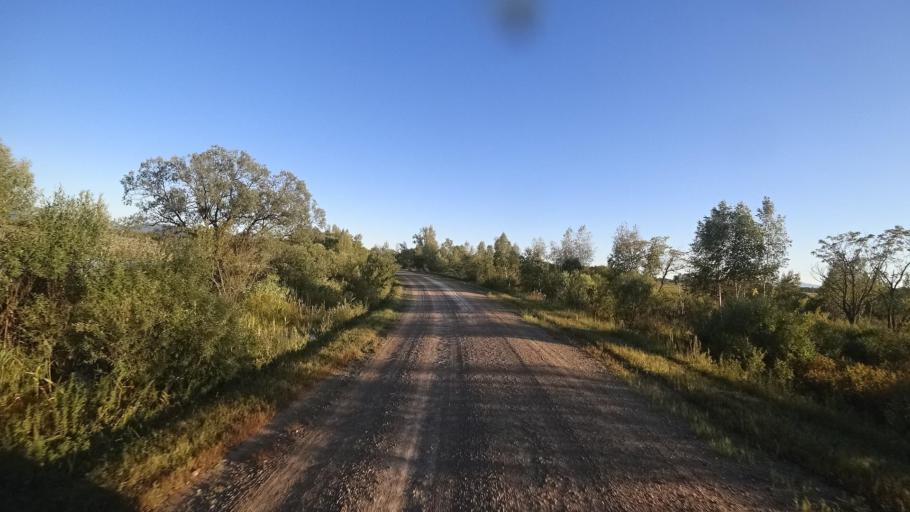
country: RU
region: Primorskiy
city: Kirovskiy
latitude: 44.7878
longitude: 133.6228
